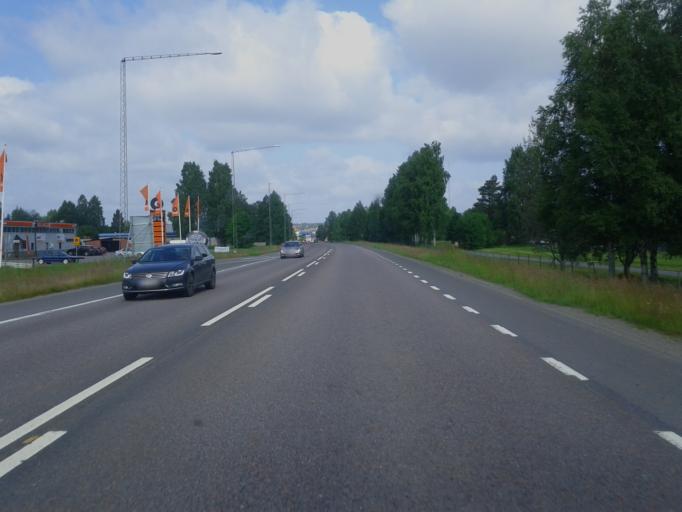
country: SE
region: Vaesterbotten
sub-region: Skelleftea Kommun
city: Skelleftea
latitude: 64.7389
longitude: 20.9646
